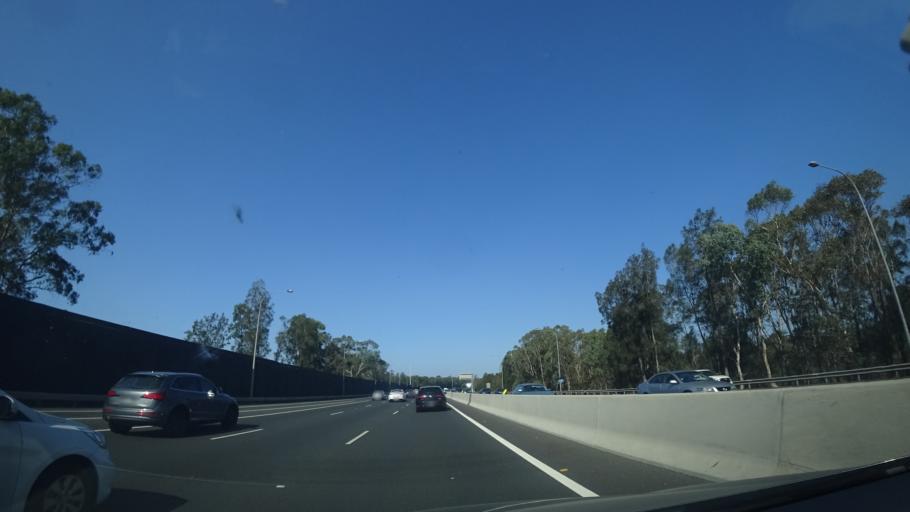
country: AU
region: New South Wales
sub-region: Bankstown
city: Milperra
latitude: -33.9440
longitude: 150.9860
